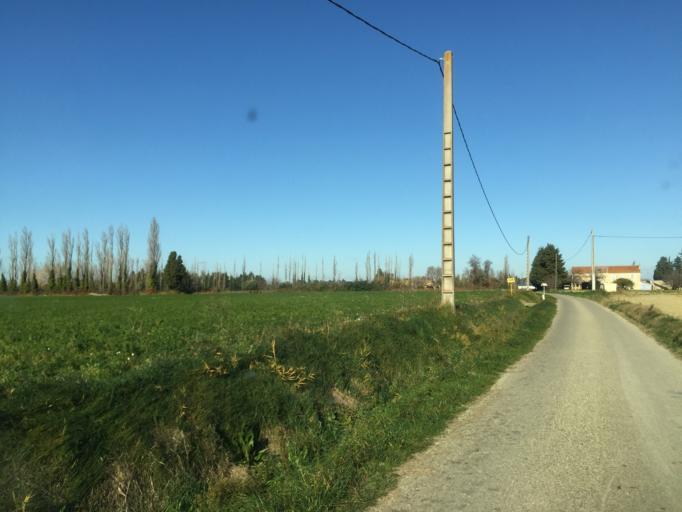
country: FR
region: Provence-Alpes-Cote d'Azur
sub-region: Departement du Vaucluse
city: Bedarrides
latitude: 44.0655
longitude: 4.9168
